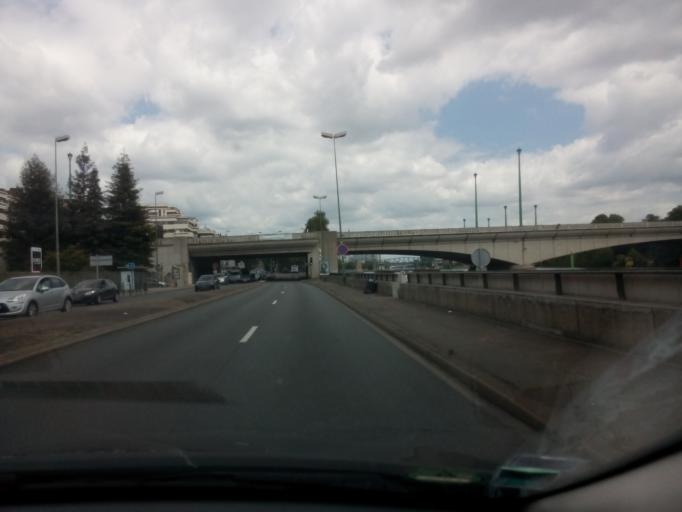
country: FR
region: Ile-de-France
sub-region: Departement des Hauts-de-Seine
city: Suresnes
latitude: 48.8662
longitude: 2.2280
